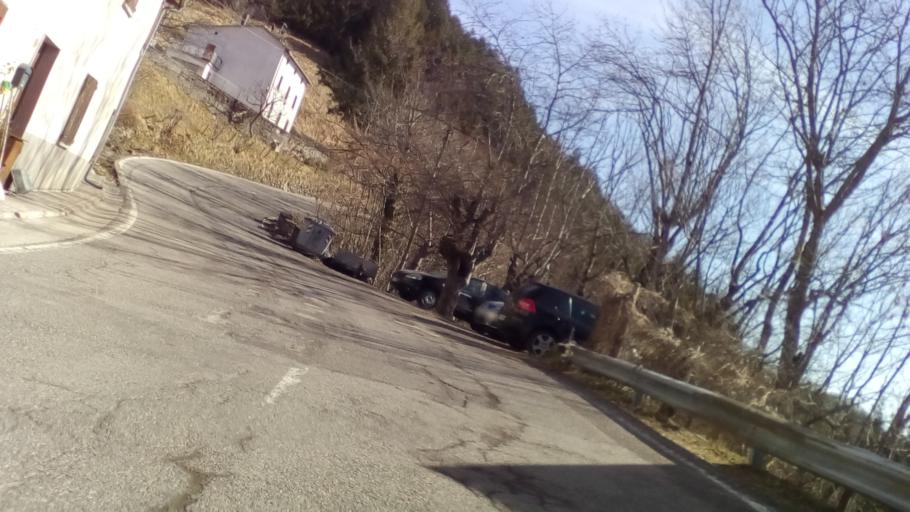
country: IT
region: Emilia-Romagna
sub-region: Provincia di Modena
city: Riolunato
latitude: 44.2575
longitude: 10.6450
